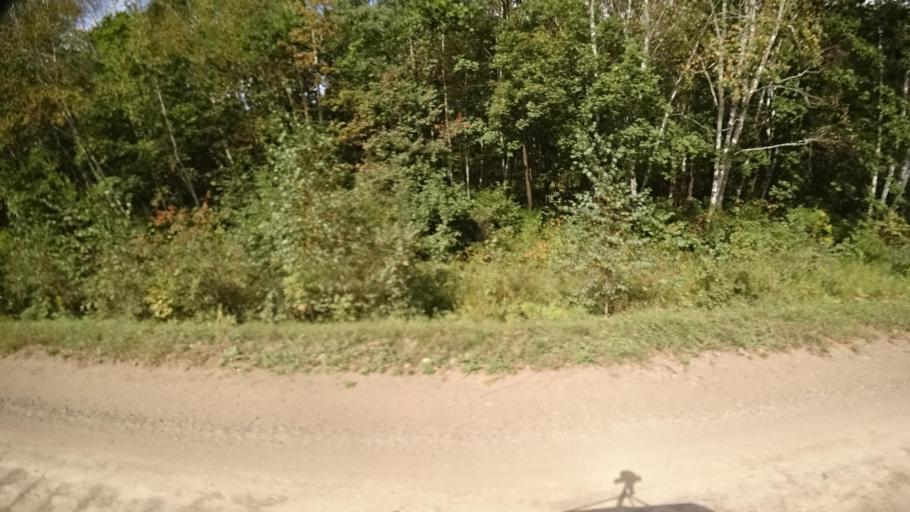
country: RU
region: Primorskiy
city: Yakovlevka
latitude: 44.7011
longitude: 133.6328
